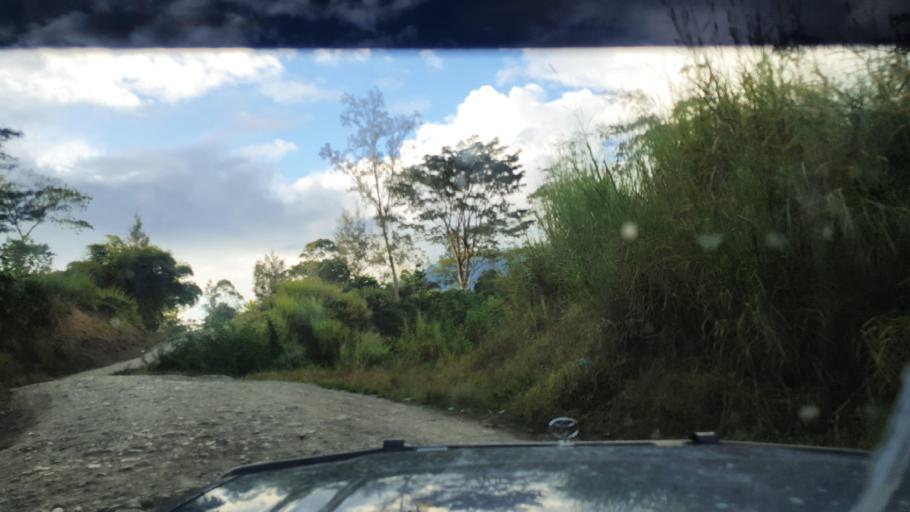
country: PG
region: Chimbu
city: Kundiawa
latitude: -5.9376
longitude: 144.8536
